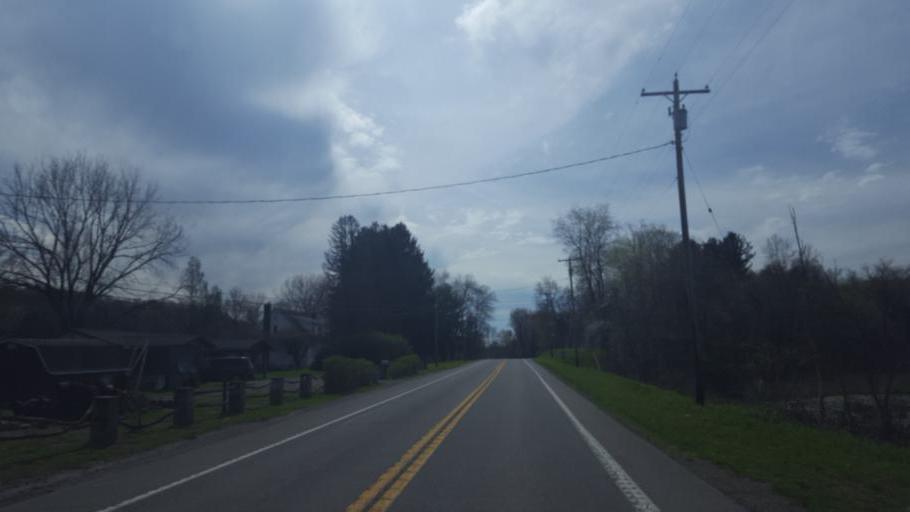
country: US
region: Pennsylvania
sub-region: Mercer County
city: Stoneboro
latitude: 41.3524
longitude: -80.0708
